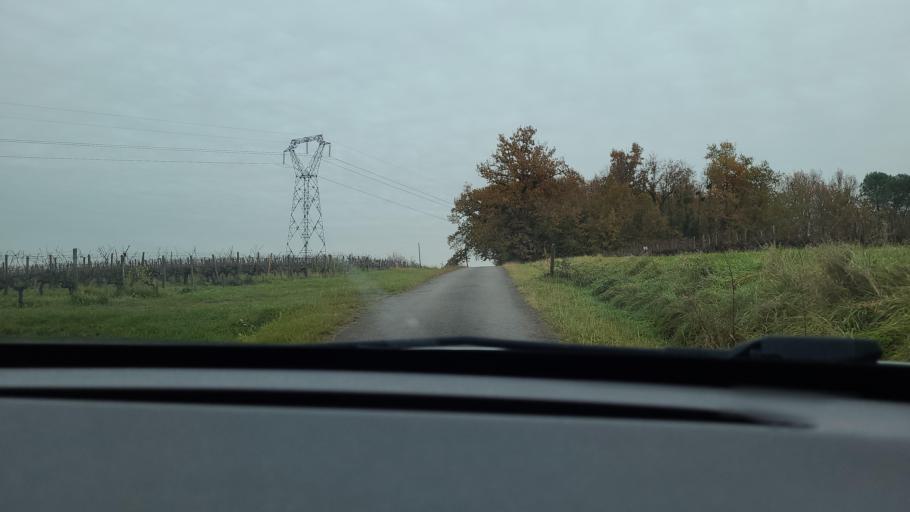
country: FR
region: Aquitaine
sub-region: Departement de la Gironde
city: Bourg
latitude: 45.0700
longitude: -0.5409
